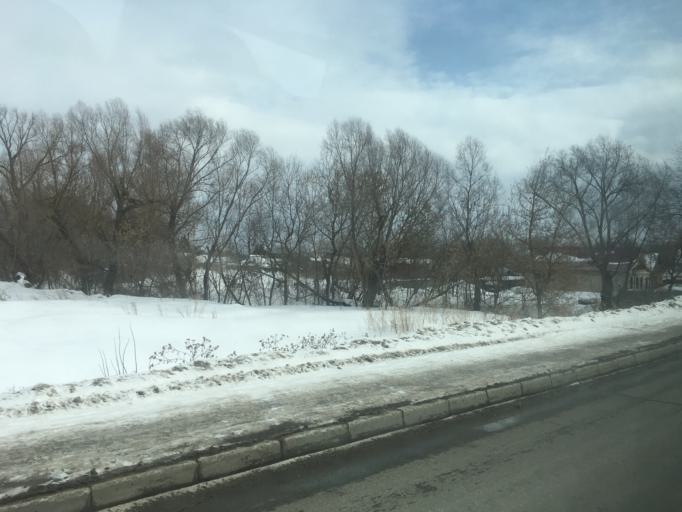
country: RU
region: Tatarstan
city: Nizhniye Vyazovyye
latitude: 55.7759
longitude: 48.5222
